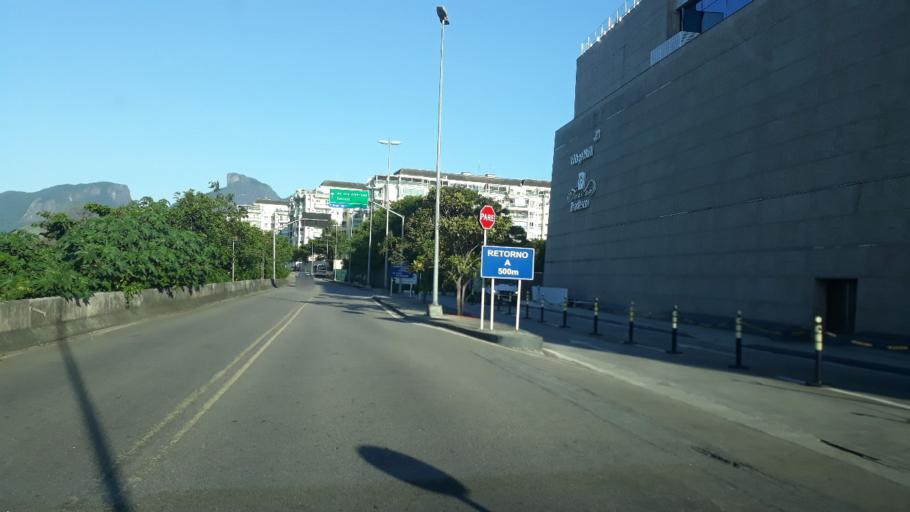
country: BR
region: Rio de Janeiro
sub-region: Rio De Janeiro
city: Rio de Janeiro
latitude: -22.9968
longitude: -43.3515
